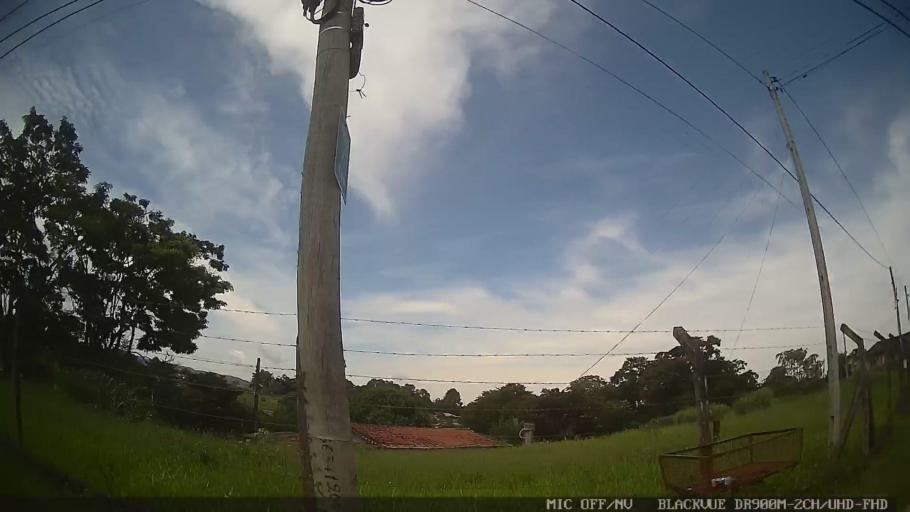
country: BR
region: Sao Paulo
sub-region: Santa Isabel
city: Santa Isabel
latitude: -23.3941
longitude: -46.1801
